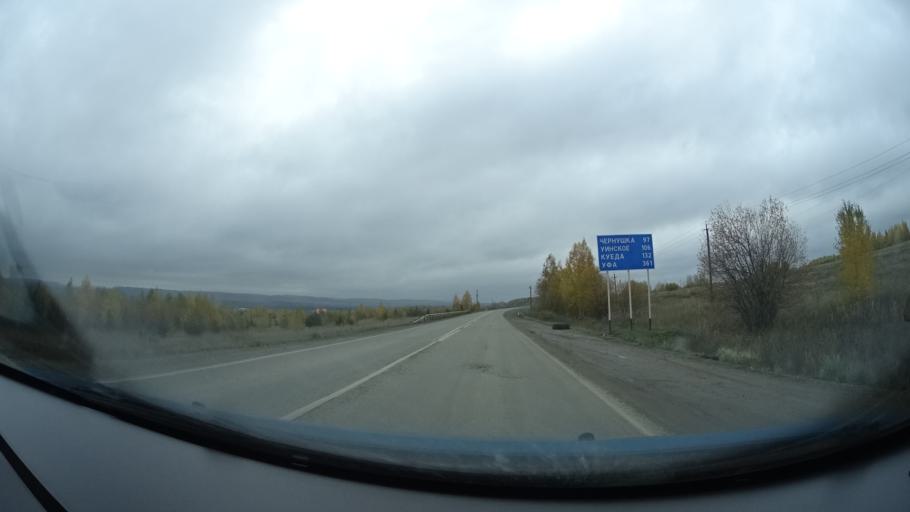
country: RU
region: Perm
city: Osa
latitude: 57.1770
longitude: 55.5317
